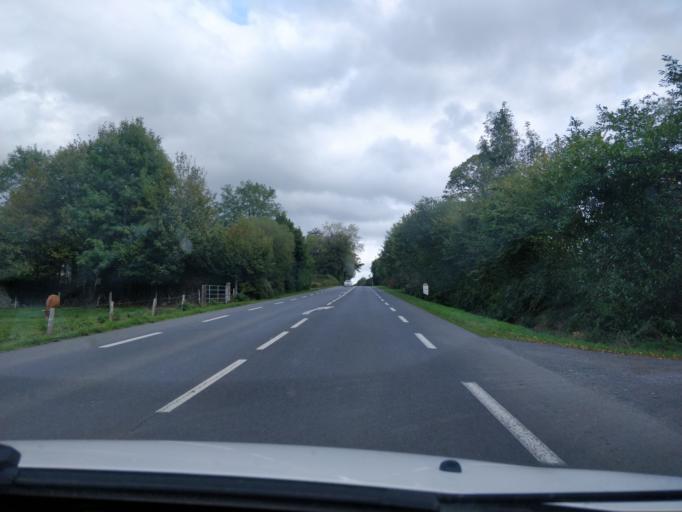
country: FR
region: Lower Normandy
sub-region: Departement du Calvados
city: Saint-Sever-Calvados
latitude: 48.8399
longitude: -0.9677
